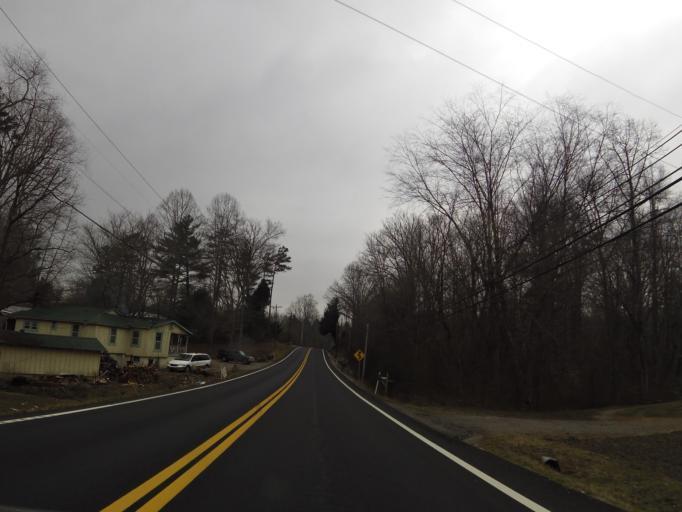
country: US
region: Tennessee
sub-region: Morgan County
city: Wartburg
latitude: 36.0782
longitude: -84.5473
